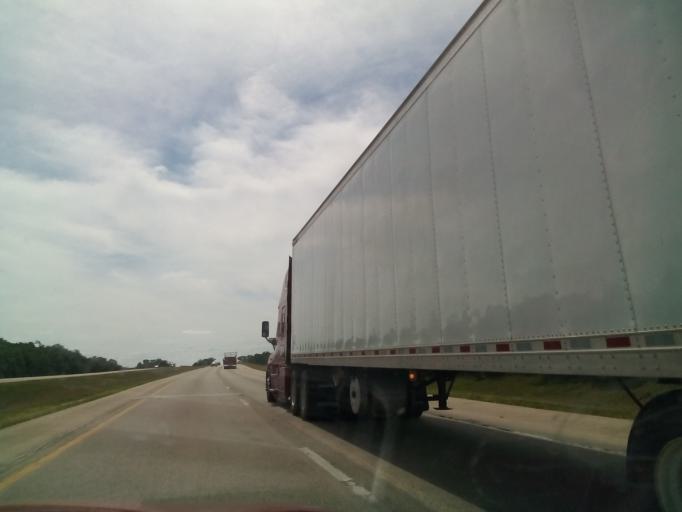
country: US
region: Illinois
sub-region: Ogle County
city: Davis Junction
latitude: 42.0543
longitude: -89.0194
